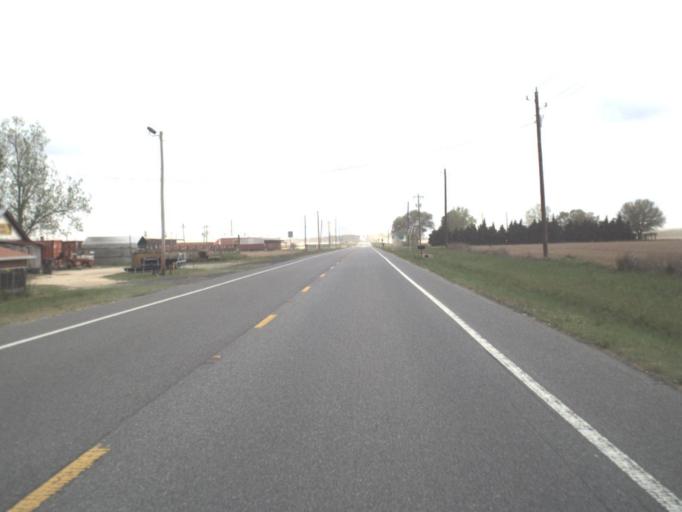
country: US
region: Florida
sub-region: Santa Rosa County
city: Point Baker
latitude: 30.7826
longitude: -87.0926
